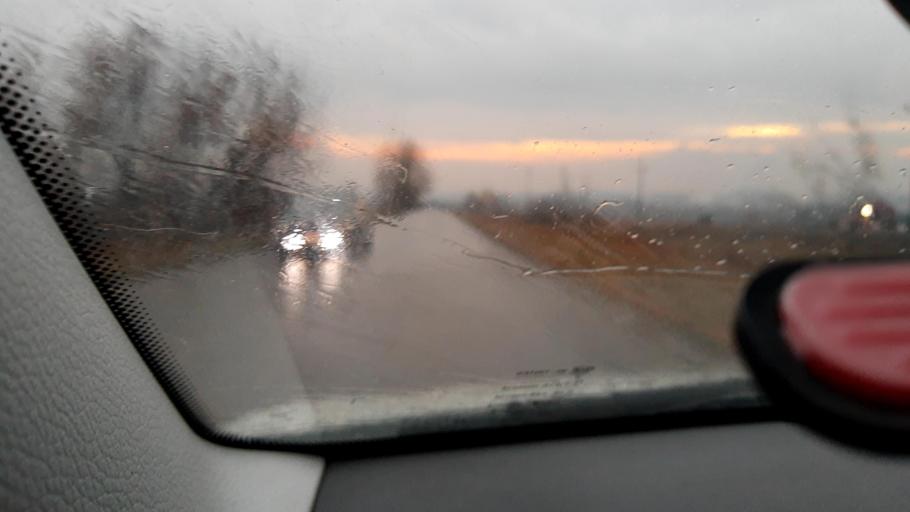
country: RU
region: Bashkortostan
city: Blagoveshchensk
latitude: 54.8926
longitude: 56.1489
